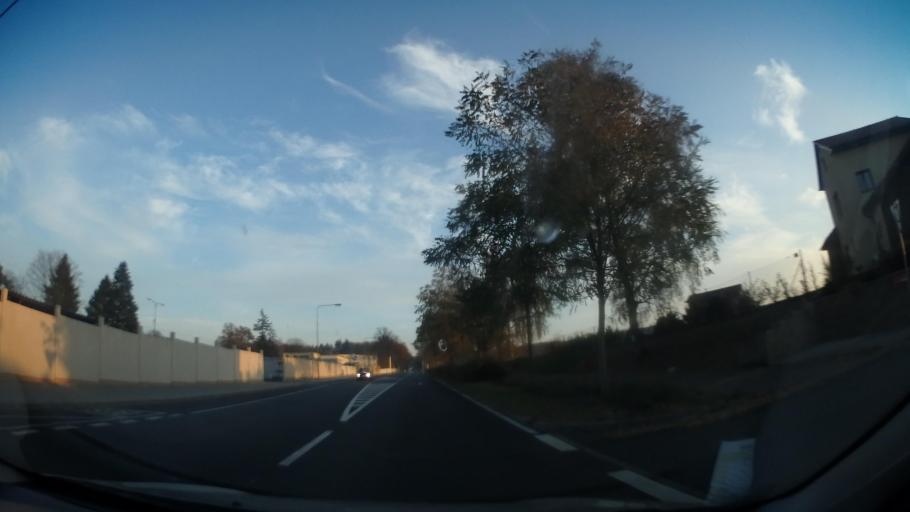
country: CZ
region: Central Bohemia
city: Vlasim
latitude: 49.6954
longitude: 14.9074
